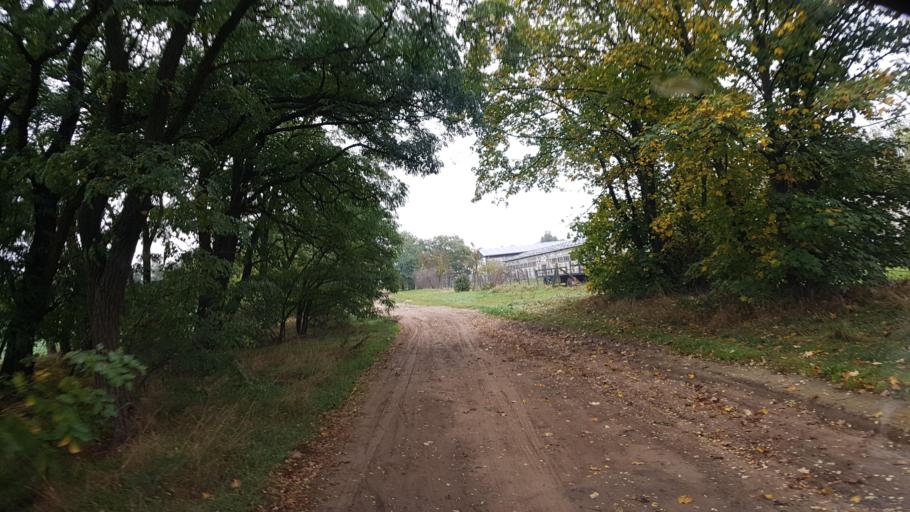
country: DE
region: Brandenburg
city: Furstenwalde
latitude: 52.4298
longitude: 14.0135
